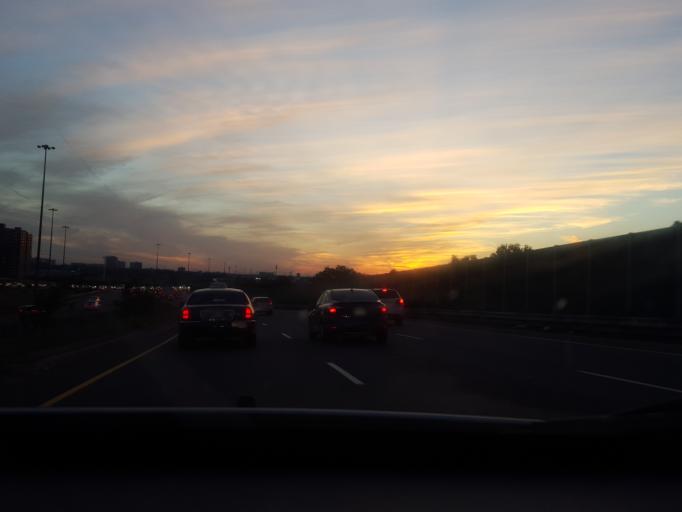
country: CA
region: Ontario
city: Concord
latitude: 43.7198
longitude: -79.4983
